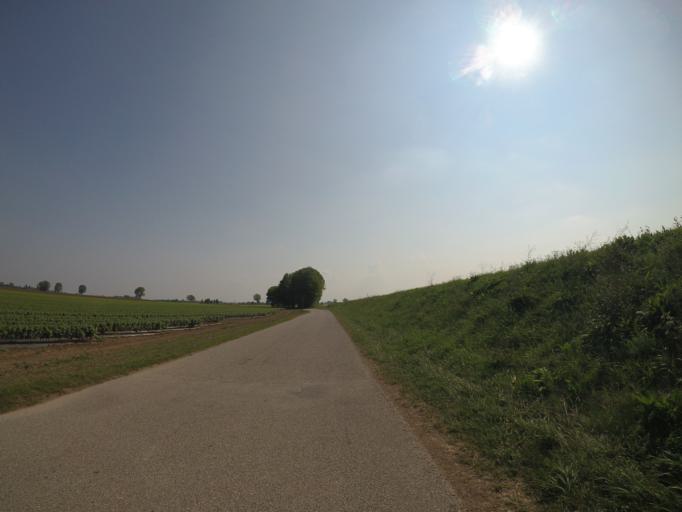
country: IT
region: Friuli Venezia Giulia
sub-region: Provincia di Udine
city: Camino al Tagliamento
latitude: 45.9293
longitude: 12.9227
